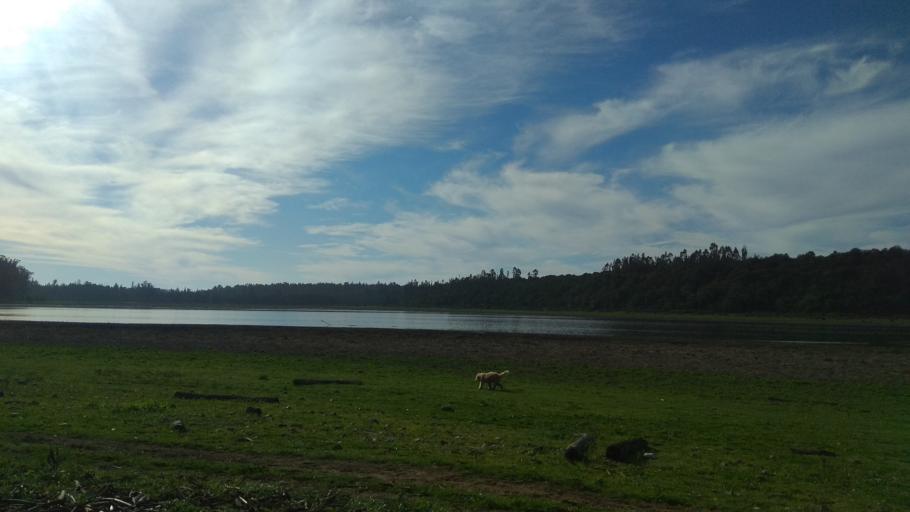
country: CL
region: Valparaiso
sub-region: San Antonio Province
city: San Antonio
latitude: -33.7649
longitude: -71.6791
